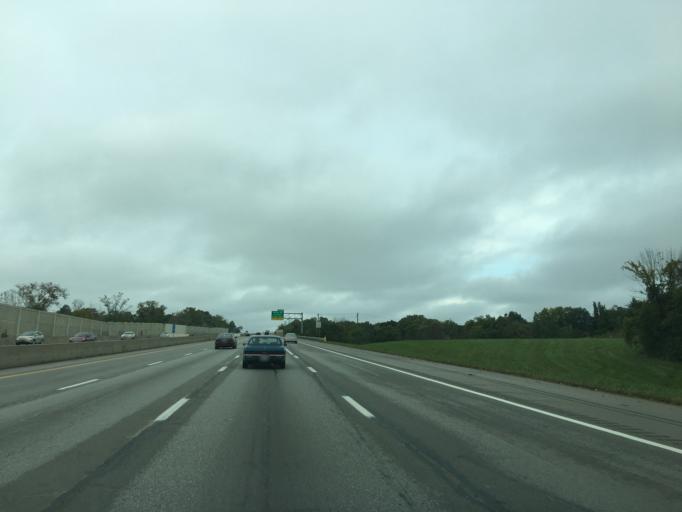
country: US
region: Ohio
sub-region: Hamilton County
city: Forest Park
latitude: 39.2972
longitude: -84.5002
